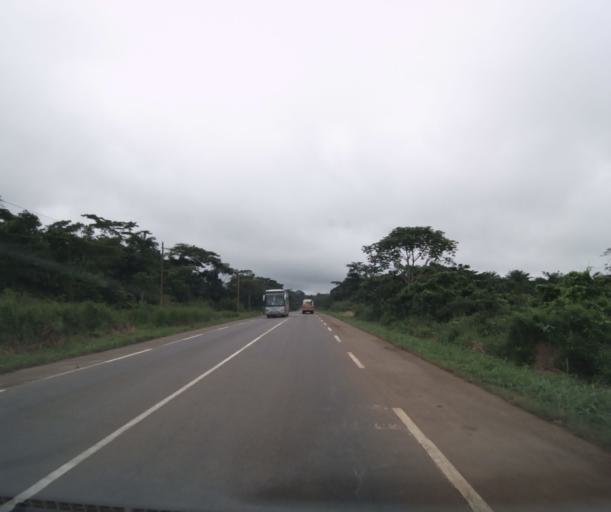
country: CM
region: Centre
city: Mbankomo
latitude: 3.7693
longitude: 11.1375
